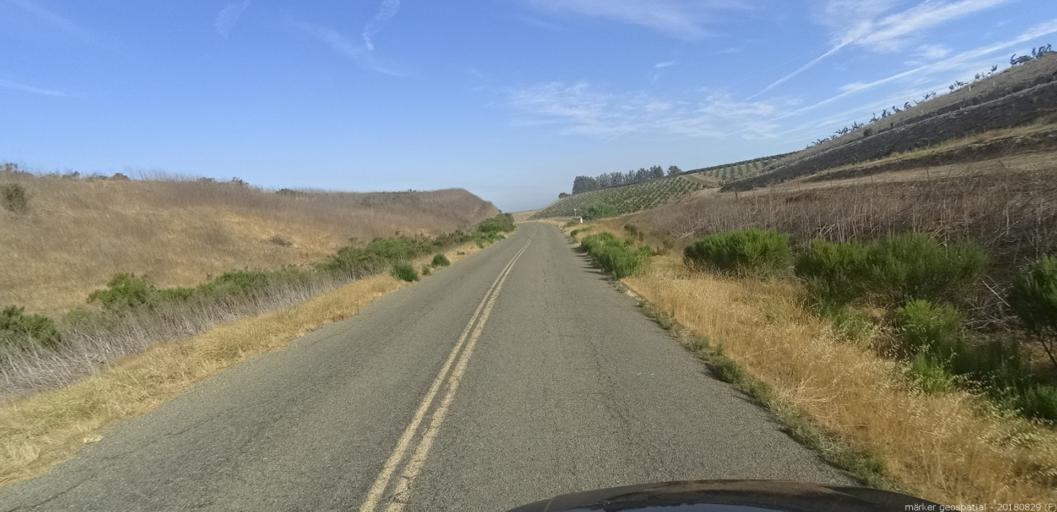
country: US
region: California
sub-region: Monterey County
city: King City
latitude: 36.0813
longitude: -121.0023
